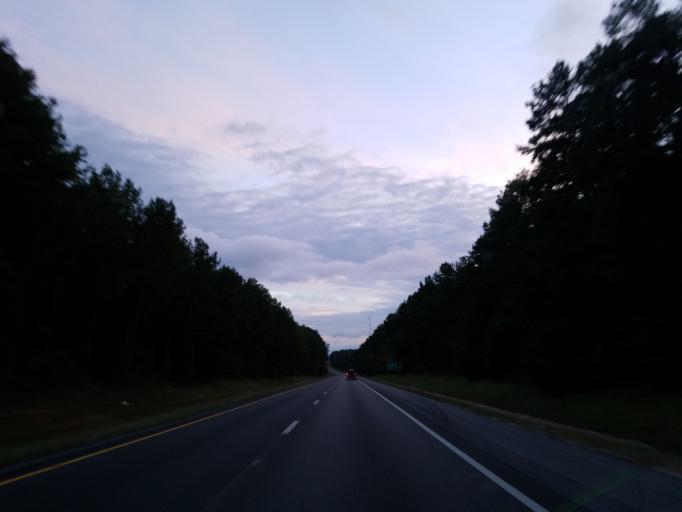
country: US
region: Mississippi
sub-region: Clarke County
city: Stonewall
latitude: 32.2577
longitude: -88.8221
